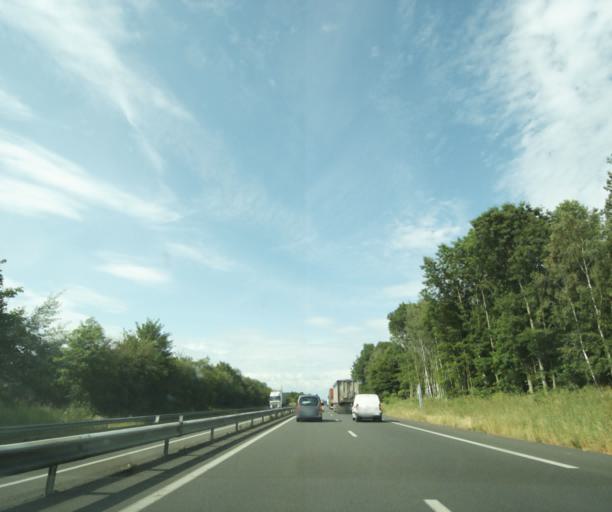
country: FR
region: Pays de la Loire
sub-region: Departement de Maine-et-Loire
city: Durtal
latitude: 47.7253
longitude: -0.2505
